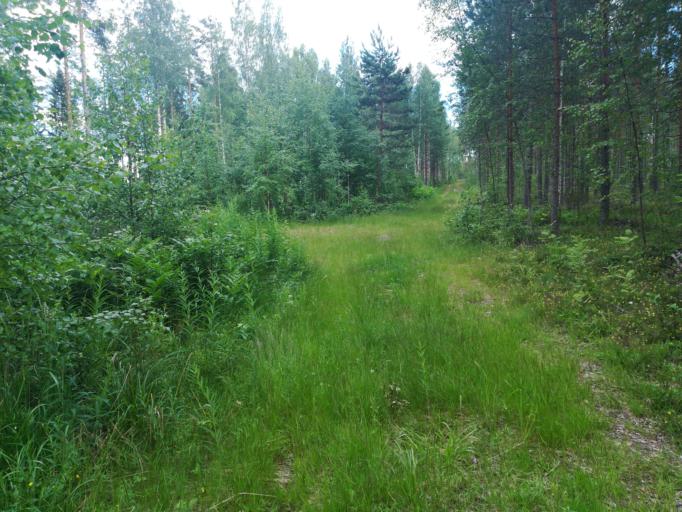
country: FI
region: South Karelia
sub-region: Lappeenranta
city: Savitaipale
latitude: 61.5027
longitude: 27.8373
